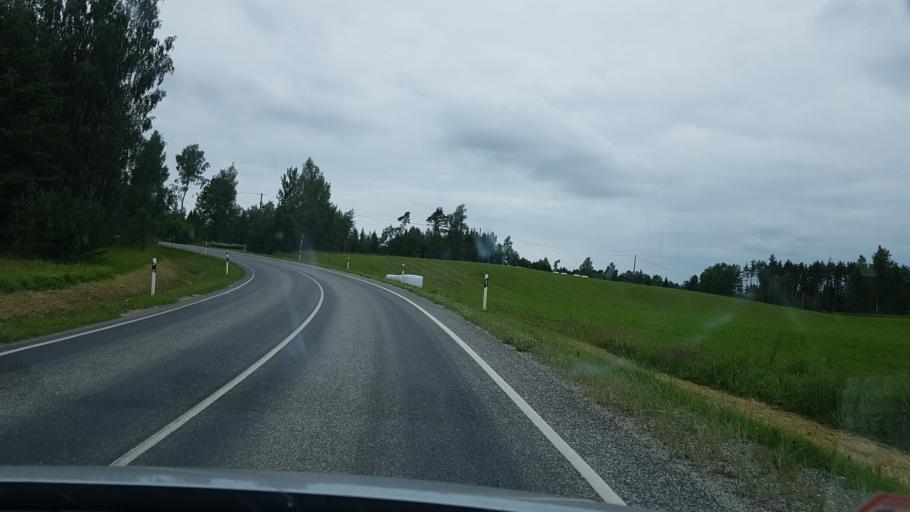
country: EE
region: Vorumaa
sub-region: Antsla vald
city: Vana-Antsla
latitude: 58.0207
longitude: 26.5863
